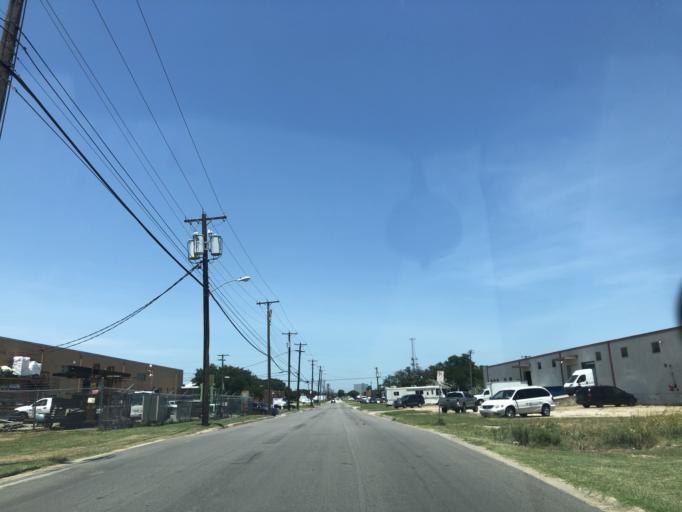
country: US
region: Texas
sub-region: Dallas County
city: Irving
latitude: 32.8160
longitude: -96.8893
